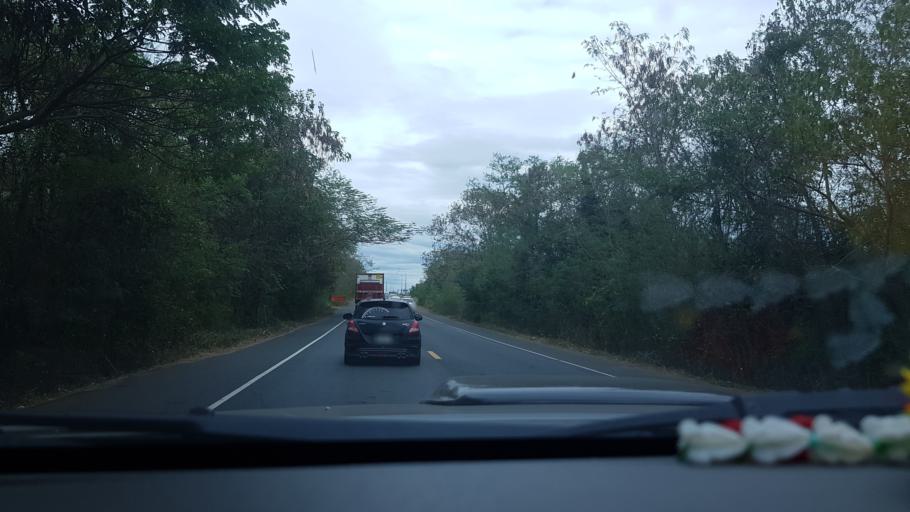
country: TH
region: Phetchabun
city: Phetchabun
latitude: 16.4832
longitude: 101.1364
